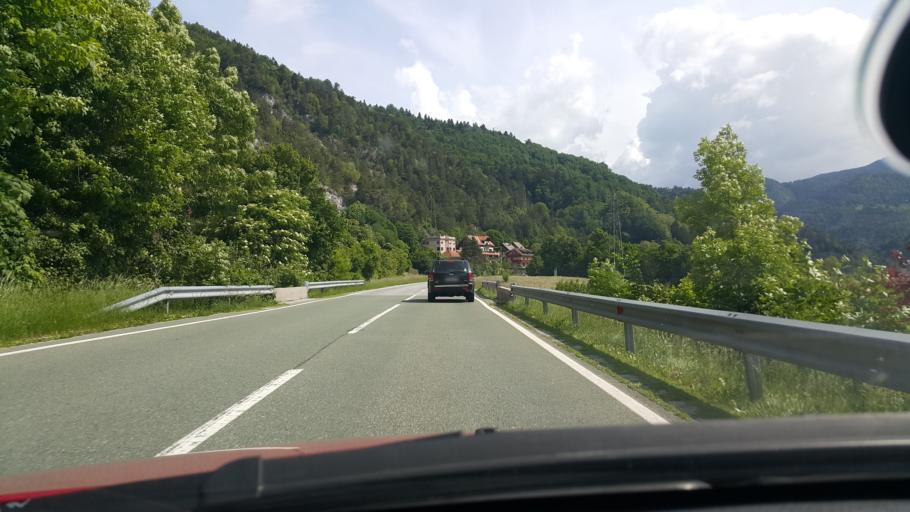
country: SI
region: Trzic
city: Bistrica pri Trzicu
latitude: 46.3562
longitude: 14.2942
